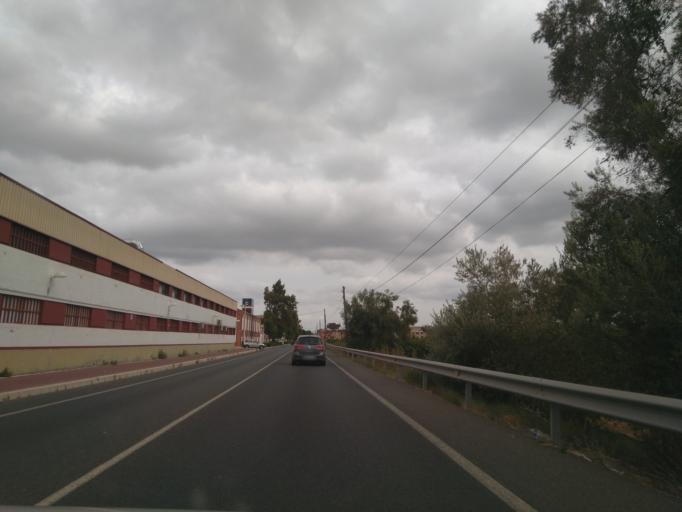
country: ES
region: Valencia
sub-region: Provincia de Valencia
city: L'Alcudia
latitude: 39.2055
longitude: -0.5086
